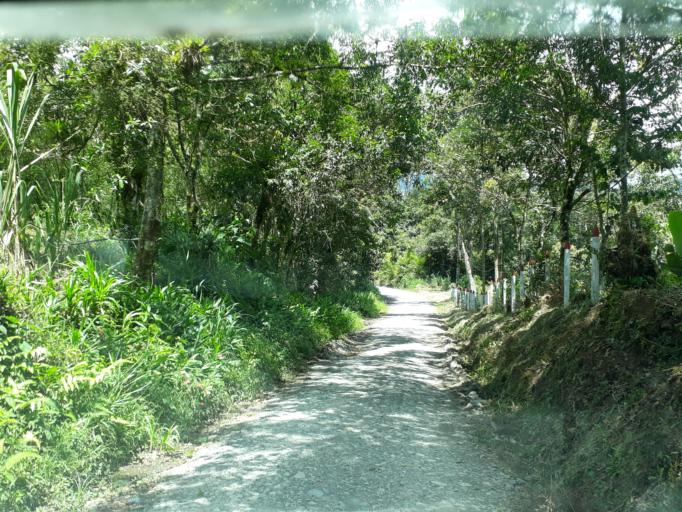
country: CO
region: Cundinamarca
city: Topaipi
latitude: 5.3584
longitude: -74.1974
